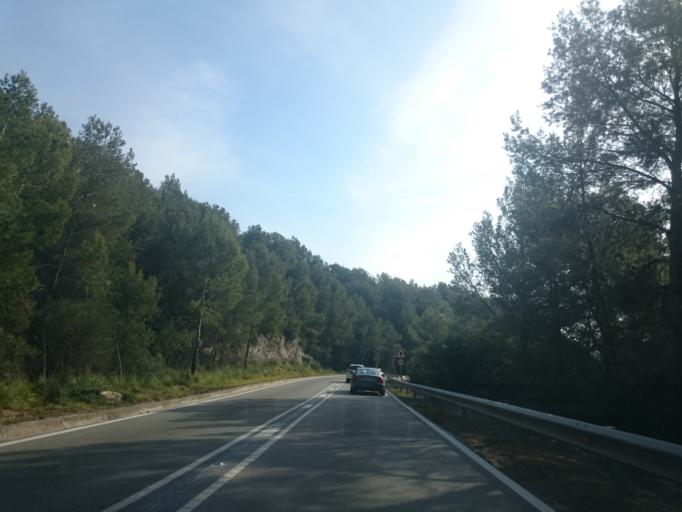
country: ES
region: Catalonia
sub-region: Provincia de Barcelona
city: Gava
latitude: 41.3111
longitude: 1.9738
